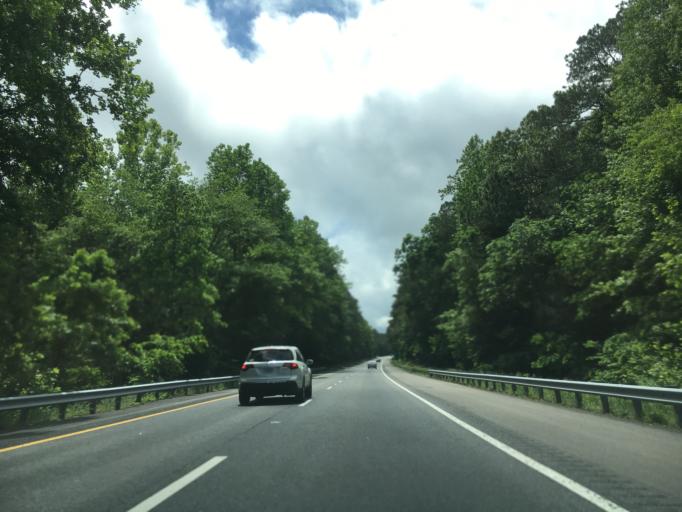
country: US
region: Virginia
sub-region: Brunswick County
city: Lawrenceville
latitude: 36.8388
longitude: -77.9264
